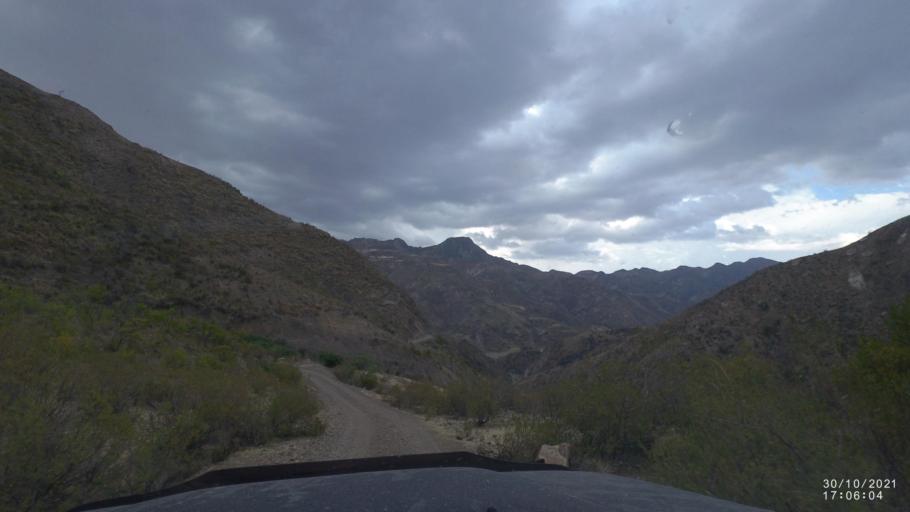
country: BO
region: Cochabamba
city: Colchani
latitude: -17.5653
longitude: -66.6280
